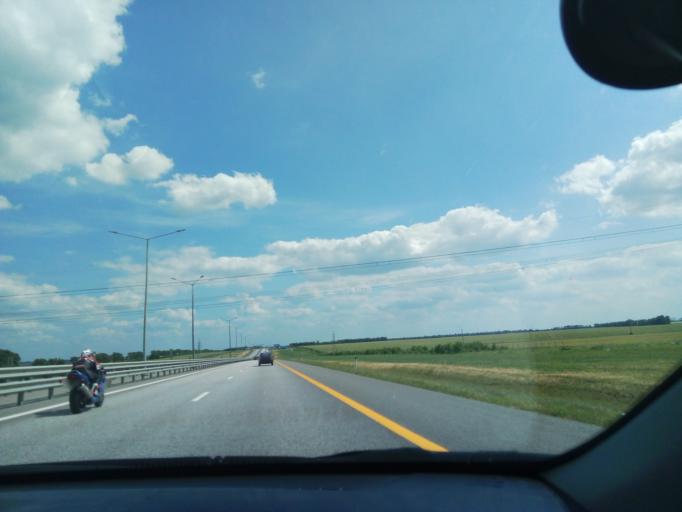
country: RU
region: Voronezj
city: Podkletnoye
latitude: 51.5497
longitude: 39.4923
